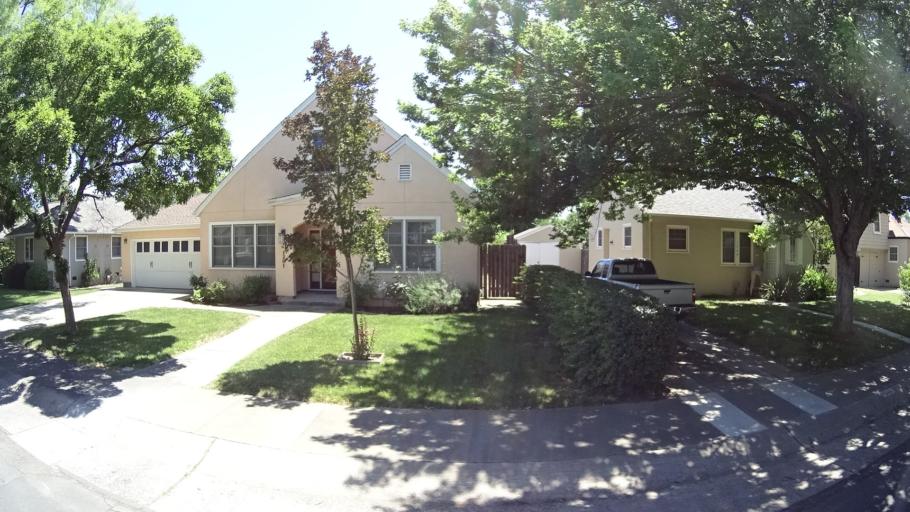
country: US
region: California
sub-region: Sacramento County
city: Sacramento
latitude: 38.5624
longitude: -121.4372
